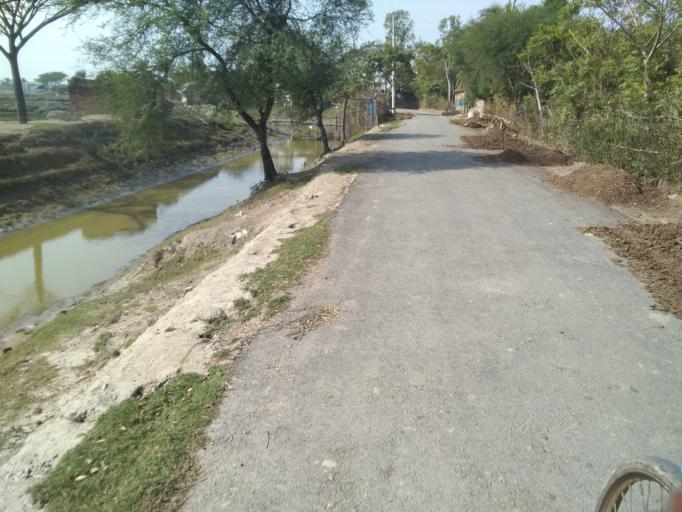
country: BD
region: Khulna
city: Satkhira
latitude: 22.6331
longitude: 89.0185
